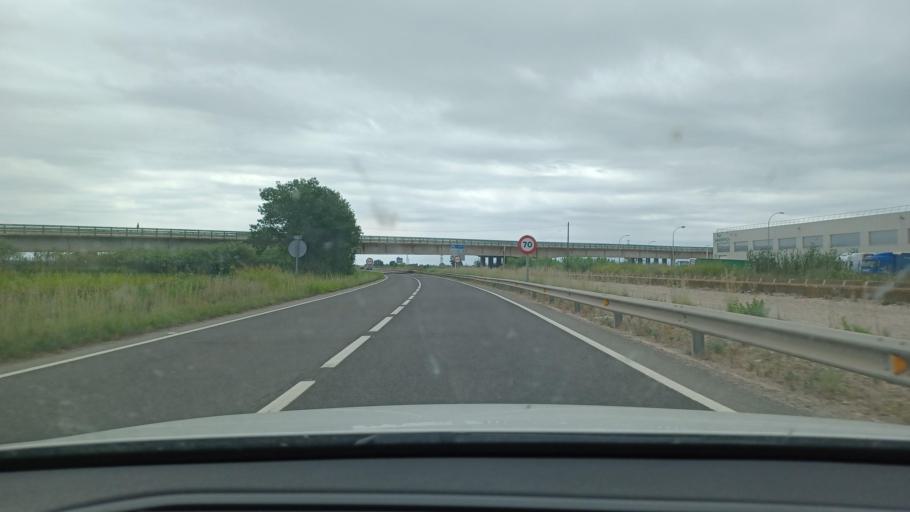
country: ES
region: Catalonia
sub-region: Provincia de Tarragona
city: Amposta
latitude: 40.7151
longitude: 0.5917
